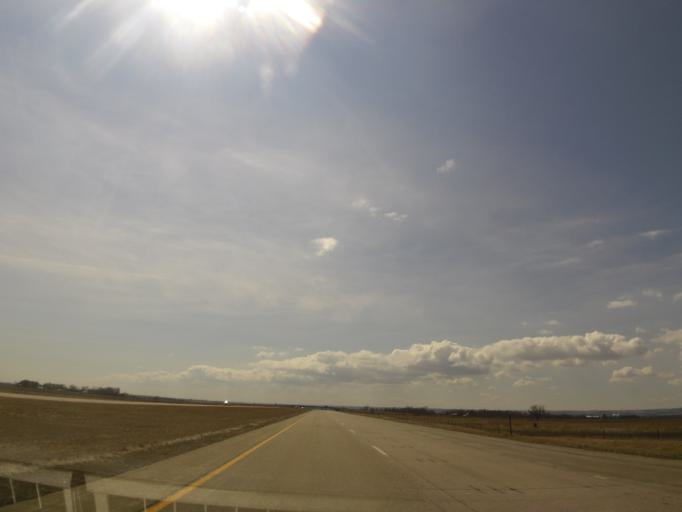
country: US
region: South Dakota
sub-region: Roberts County
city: Sisseton
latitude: 45.6987
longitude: -96.9655
